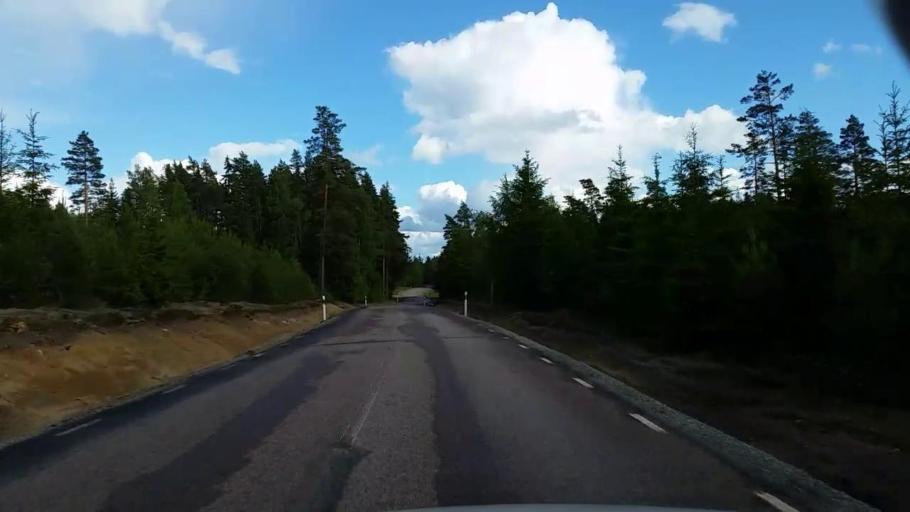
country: SE
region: Vaestmanland
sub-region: Fagersta Kommun
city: Fagersta
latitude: 59.8882
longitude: 15.8273
